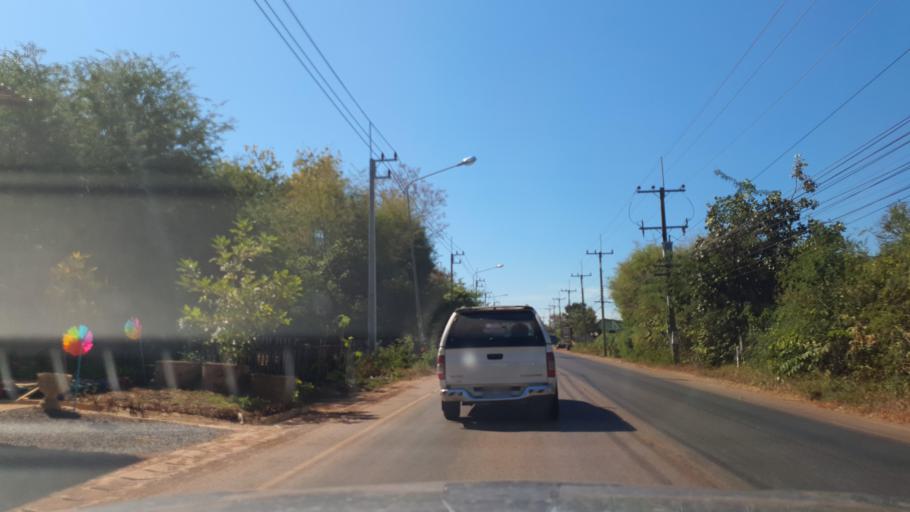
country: TH
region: Sakon Nakhon
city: Phon Na Kaeo
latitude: 17.2625
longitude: 104.1908
